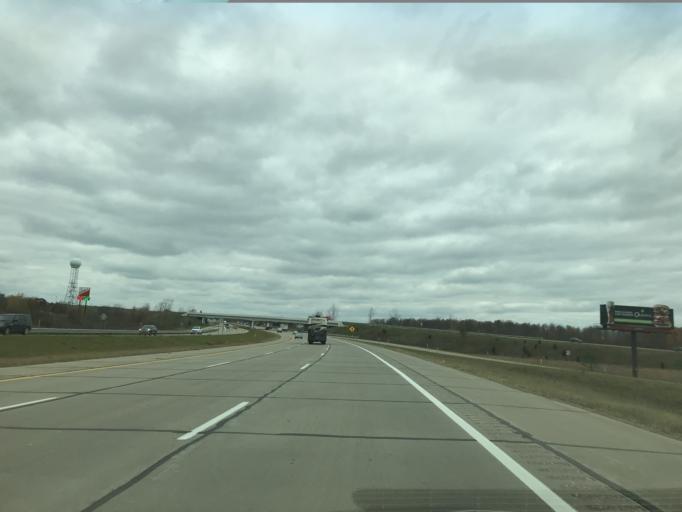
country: US
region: Michigan
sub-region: Clinton County
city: Wacousta
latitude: 42.7868
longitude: -84.6726
